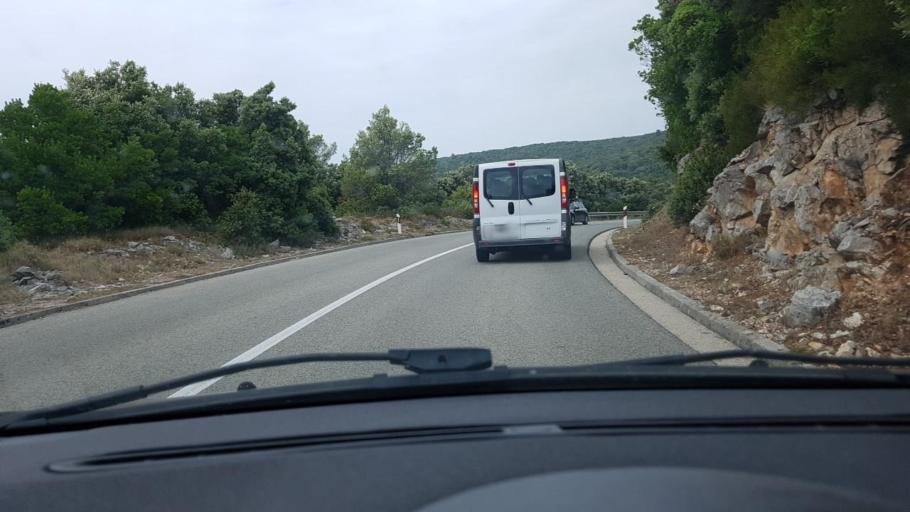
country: HR
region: Dubrovacko-Neretvanska
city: Smokvica
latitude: 42.9448
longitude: 17.0032
